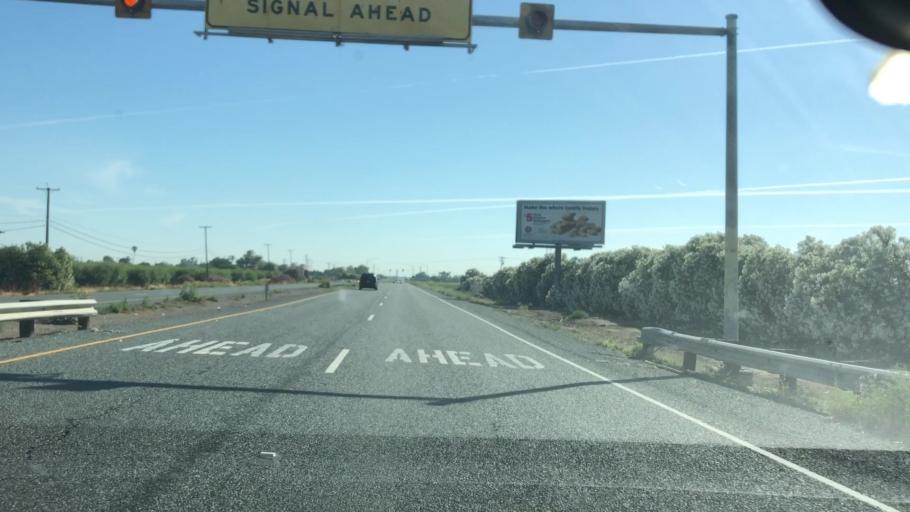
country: US
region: California
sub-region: San Joaquin County
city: Tracy
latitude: 37.7433
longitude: -121.3651
